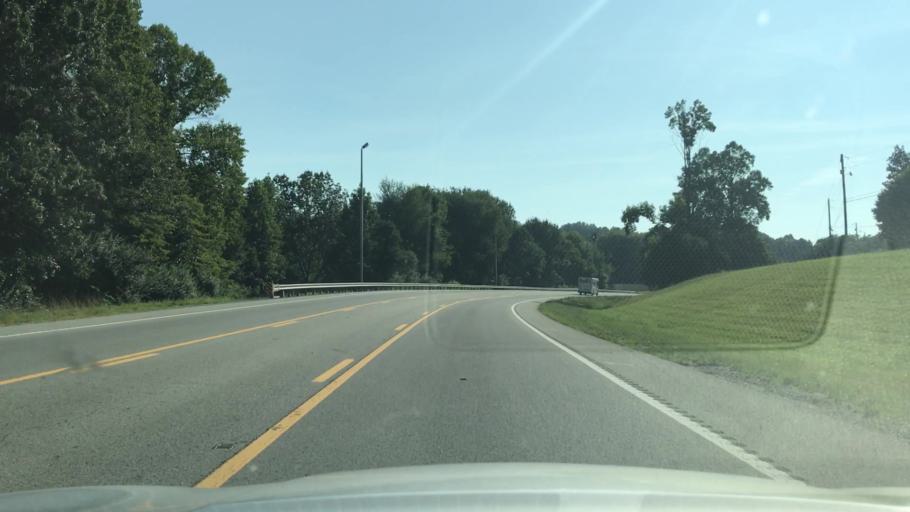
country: US
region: Tennessee
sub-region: Overton County
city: Livingston
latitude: 36.3977
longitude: -85.3109
